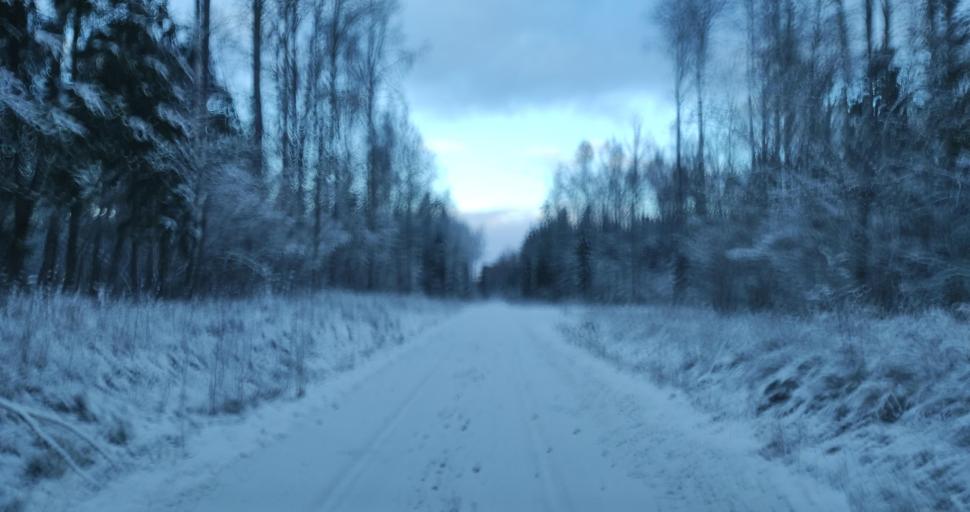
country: LV
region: Skrunda
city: Skrunda
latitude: 56.5744
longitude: 21.9204
